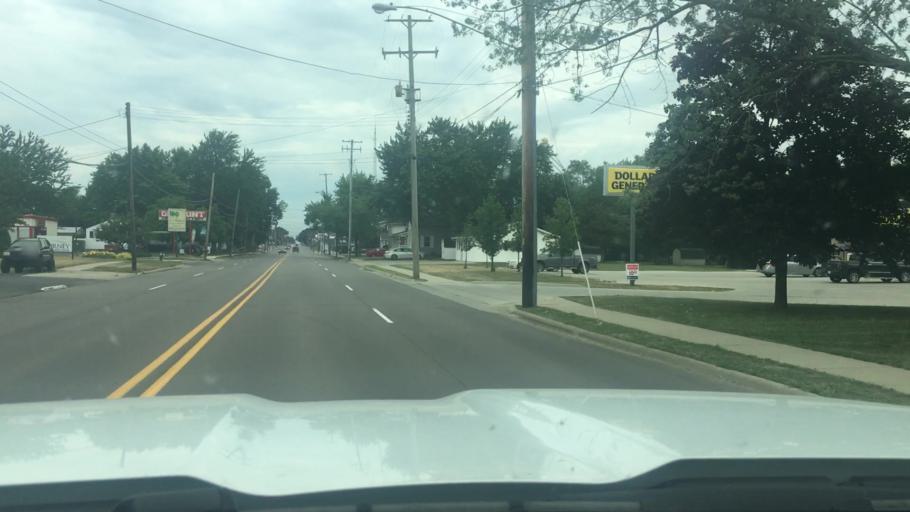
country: US
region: Michigan
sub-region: Clinton County
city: Fowler
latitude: 43.0019
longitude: -84.7342
